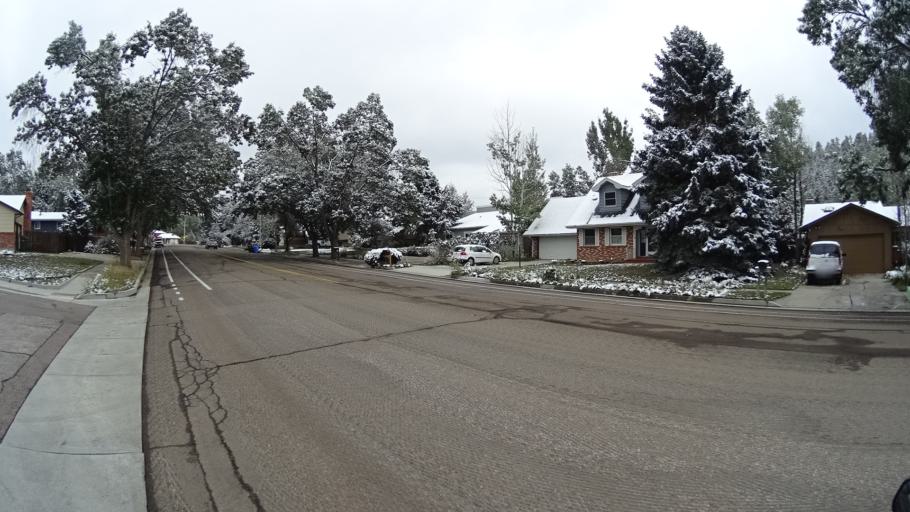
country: US
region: Colorado
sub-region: El Paso County
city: Colorado Springs
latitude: 38.8906
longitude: -104.7768
